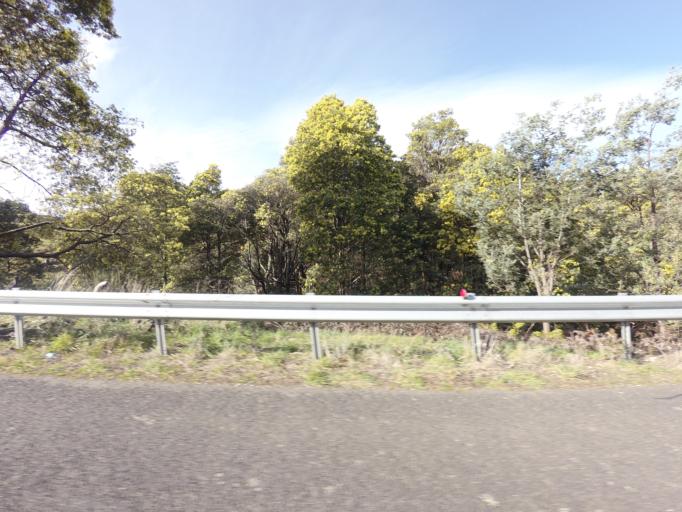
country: AU
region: Tasmania
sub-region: Kingborough
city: Kettering
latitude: -43.1724
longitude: 147.1671
